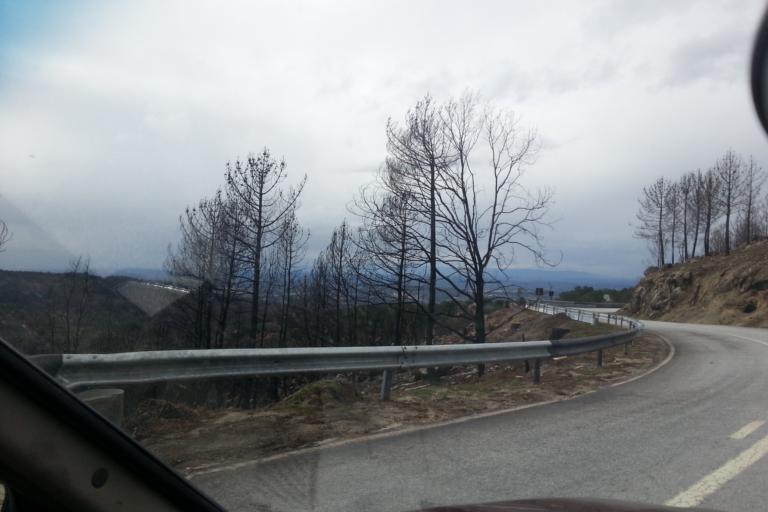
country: PT
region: Guarda
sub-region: Manteigas
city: Manteigas
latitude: 40.4712
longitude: -7.5919
